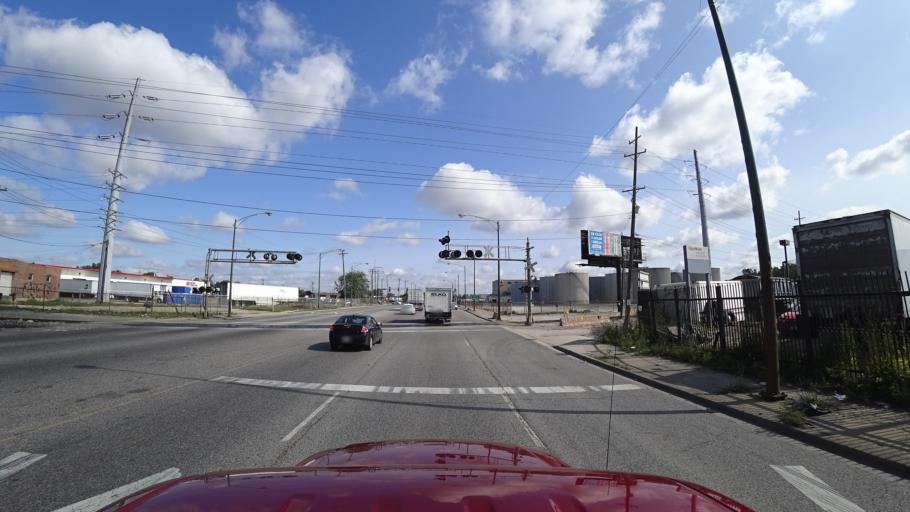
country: US
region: Illinois
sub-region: Cook County
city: Cicero
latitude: 41.8204
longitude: -87.7434
